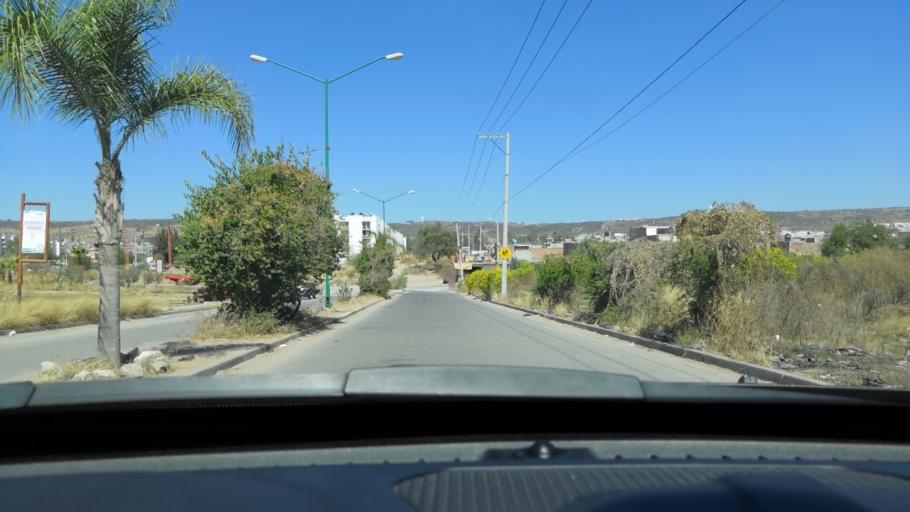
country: MX
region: Guanajuato
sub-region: Leon
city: Centro Familiar la Soledad
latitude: 21.1424
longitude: -101.7492
